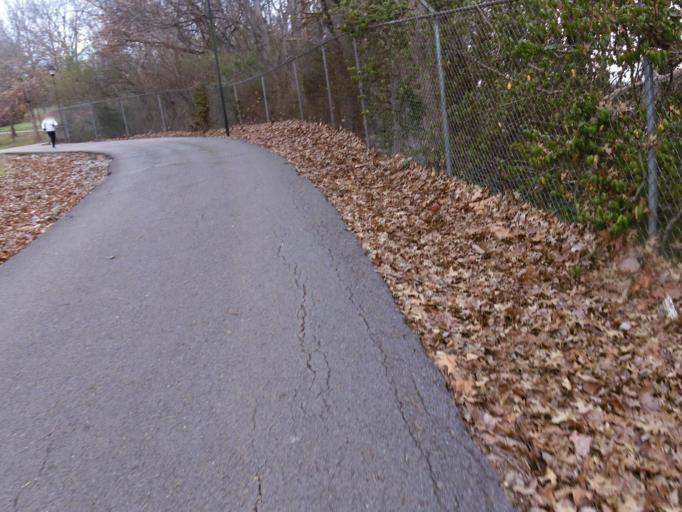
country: US
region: Tennessee
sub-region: Knox County
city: Knoxville
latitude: 35.9237
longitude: -83.9868
